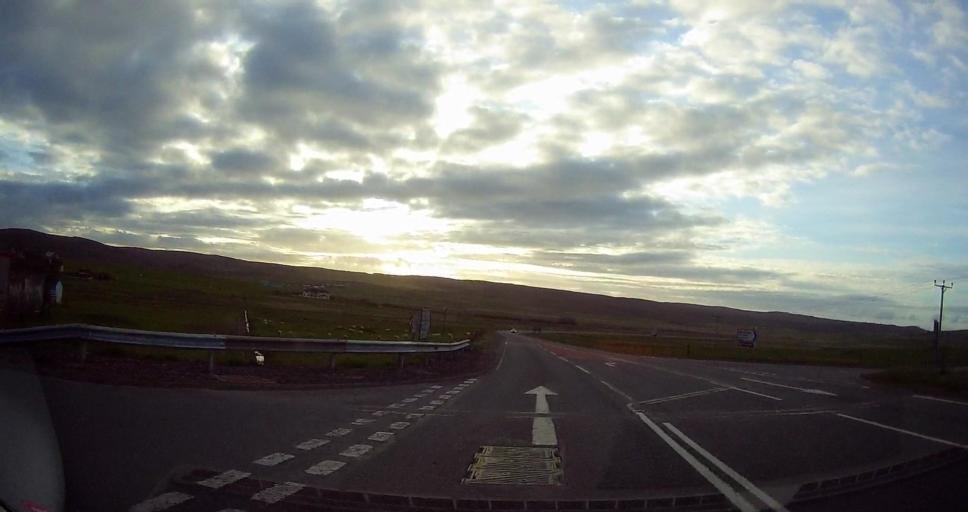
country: GB
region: Scotland
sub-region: Shetland Islands
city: Lerwick
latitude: 60.1860
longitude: -1.2260
